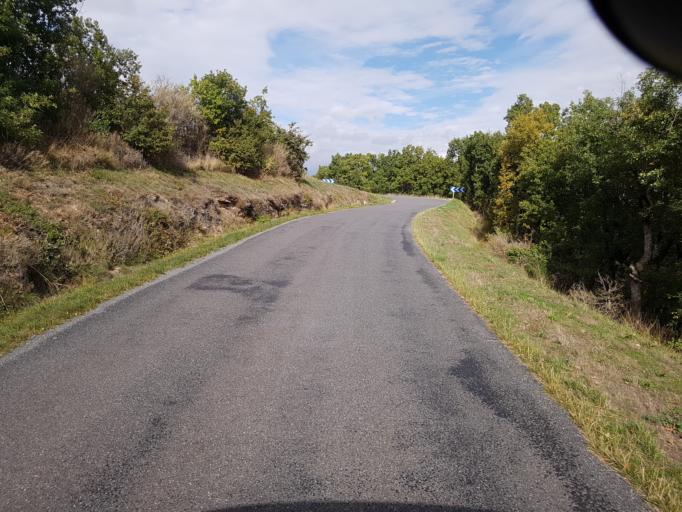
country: FR
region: Midi-Pyrenees
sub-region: Departement de l'Aveyron
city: Saint-Affrique
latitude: 43.9983
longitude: 2.9497
